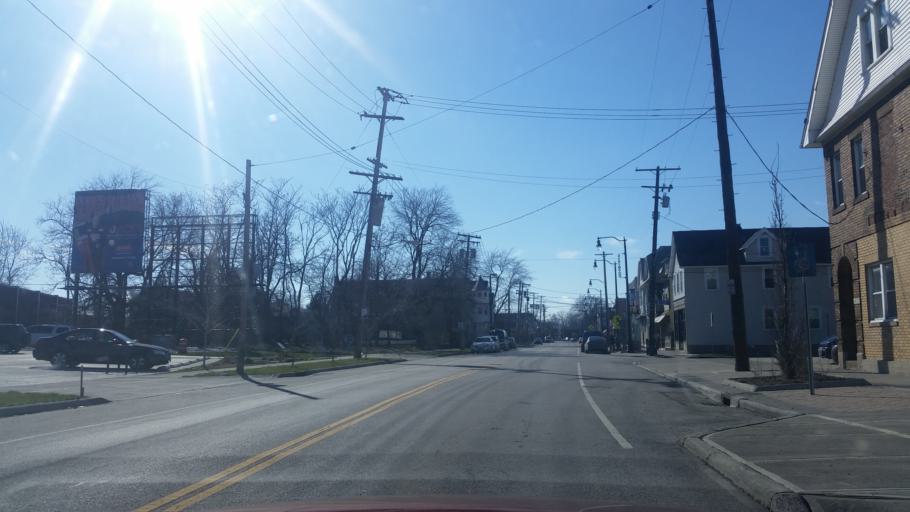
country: US
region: Ohio
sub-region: Cuyahoga County
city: East Cleveland
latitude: 41.5713
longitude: -81.5677
